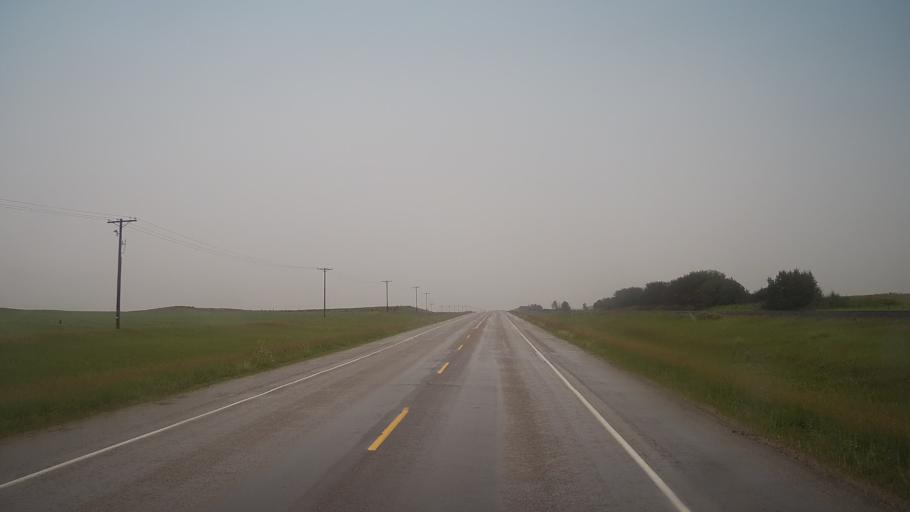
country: CA
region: Saskatchewan
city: Biggar
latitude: 52.0912
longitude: -108.0523
